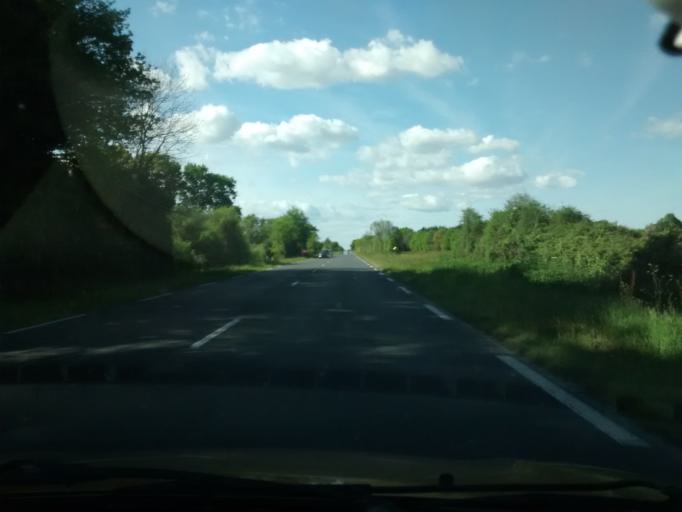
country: FR
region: Pays de la Loire
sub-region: Departement de la Loire-Atlantique
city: Geneston
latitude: 47.0755
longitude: -1.5223
